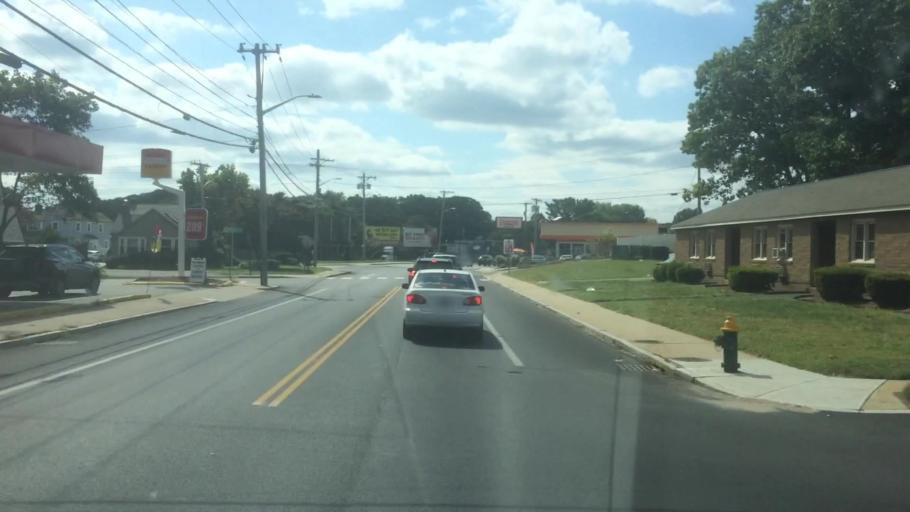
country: US
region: Rhode Island
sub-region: Providence County
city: Cranston
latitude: 41.7723
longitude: -71.4089
